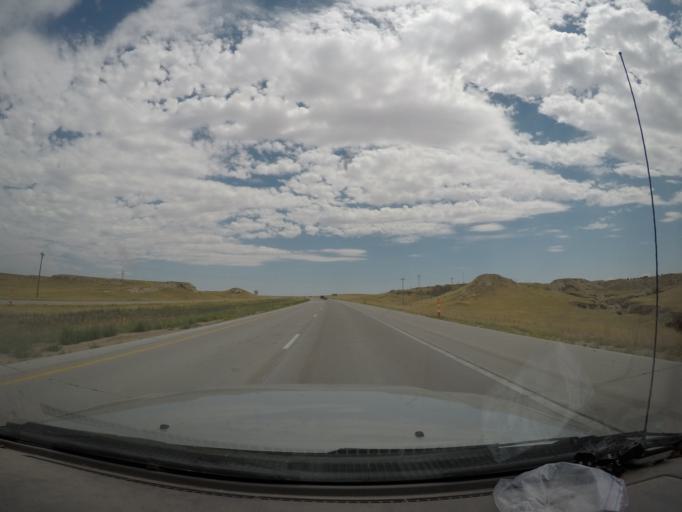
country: US
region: Nebraska
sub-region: Cheyenne County
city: Sidney
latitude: 41.1175
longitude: -103.0133
